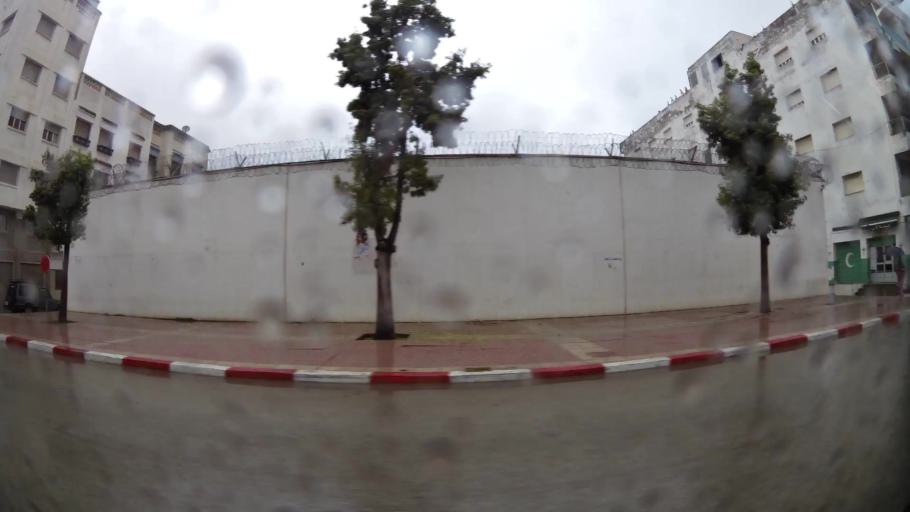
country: MA
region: Taza-Al Hoceima-Taounate
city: Al Hoceima
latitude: 35.2479
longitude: -3.9332
